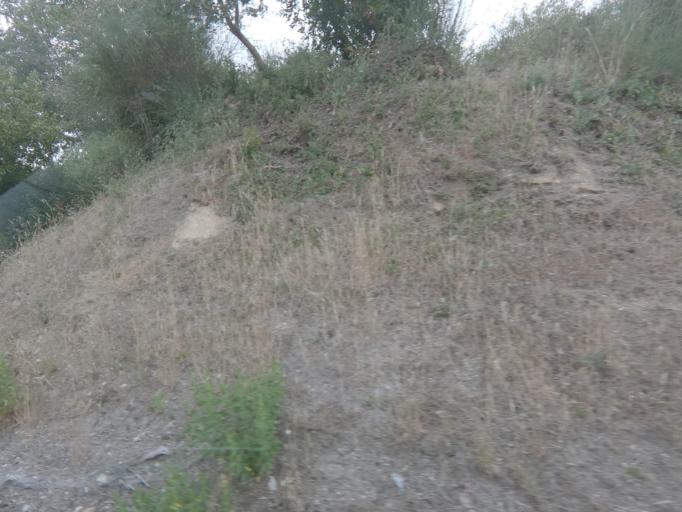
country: PT
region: Coimbra
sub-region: Condeixa-A-Nova
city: Condeixa-a-Nova
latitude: 40.1396
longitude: -8.4673
